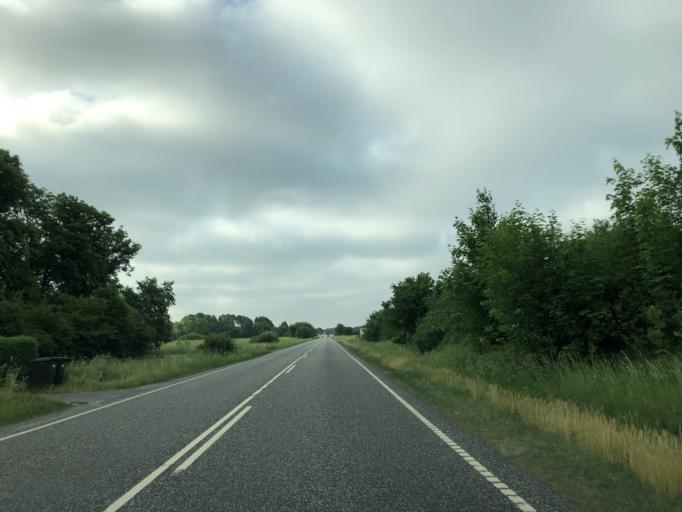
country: DK
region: South Denmark
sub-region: Vejle Kommune
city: Give
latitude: 55.8062
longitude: 9.2588
